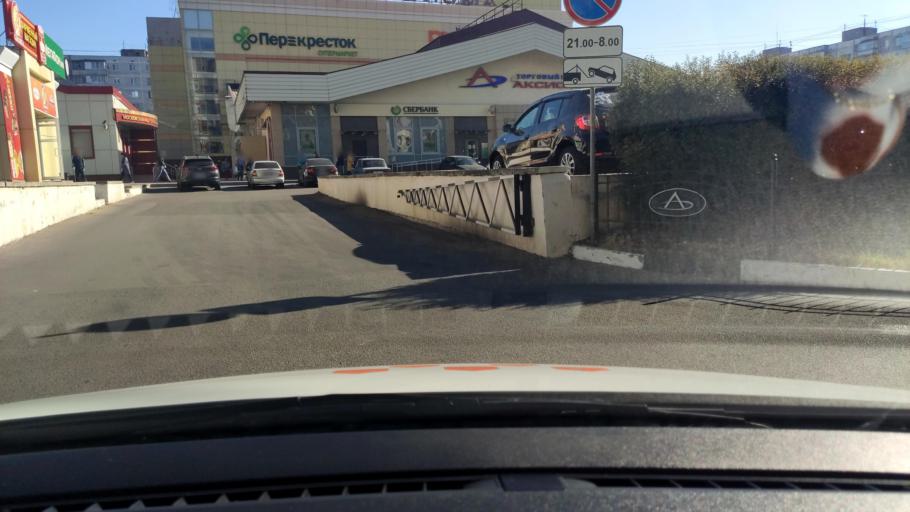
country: RU
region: Voronezj
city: Podgornoye
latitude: 51.7063
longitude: 39.1480
